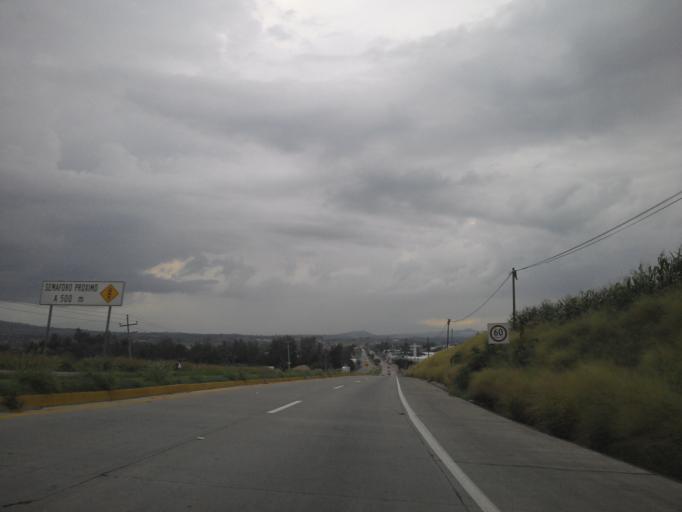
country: MX
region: Jalisco
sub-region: Zapotlanejo
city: La Mezquitera
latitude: 20.5915
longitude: -103.1104
